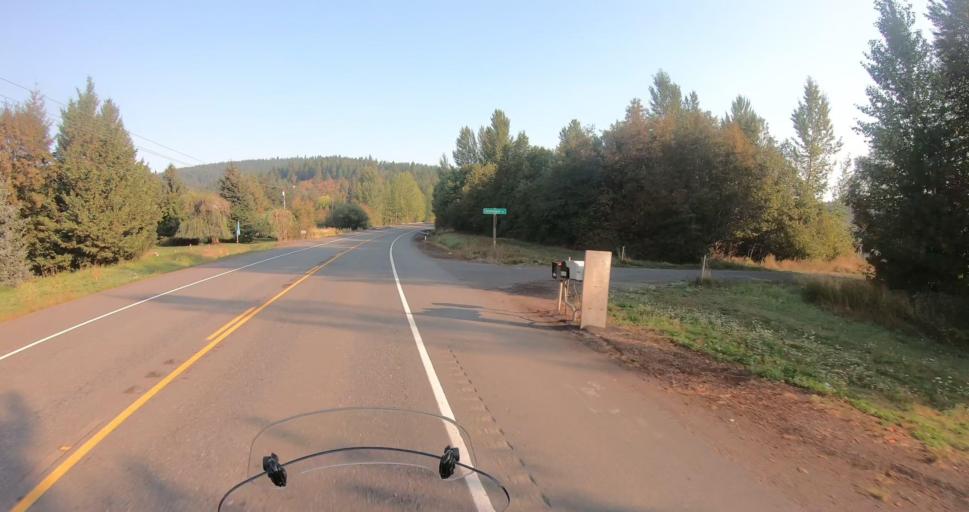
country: US
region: Oregon
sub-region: Hood River County
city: Odell
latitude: 45.5543
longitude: -121.5684
